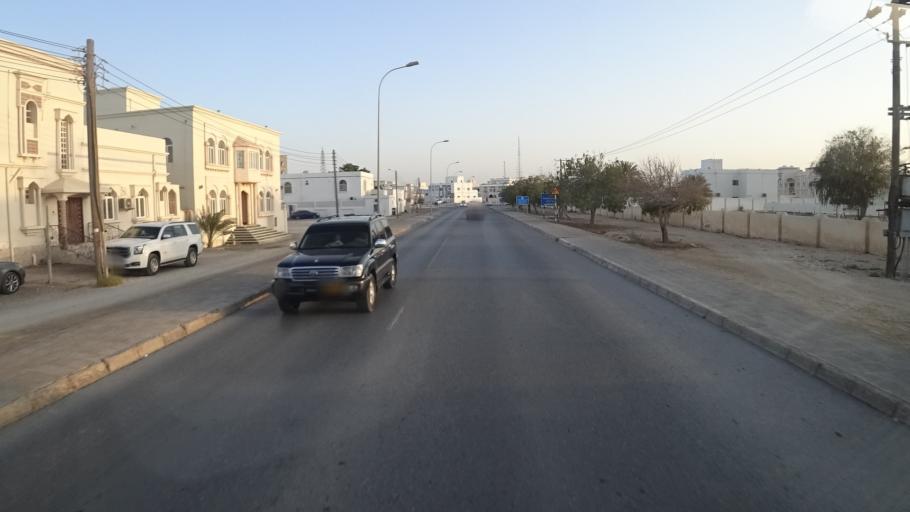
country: OM
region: Ash Sharqiyah
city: Sur
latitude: 22.5861
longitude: 59.5055
